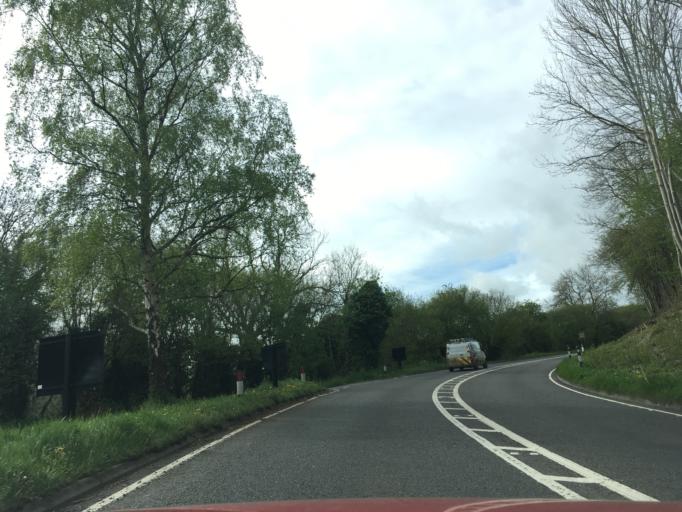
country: GB
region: England
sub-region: Bath and North East Somerset
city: Peasedown Saint John
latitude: 51.3310
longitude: -2.4088
